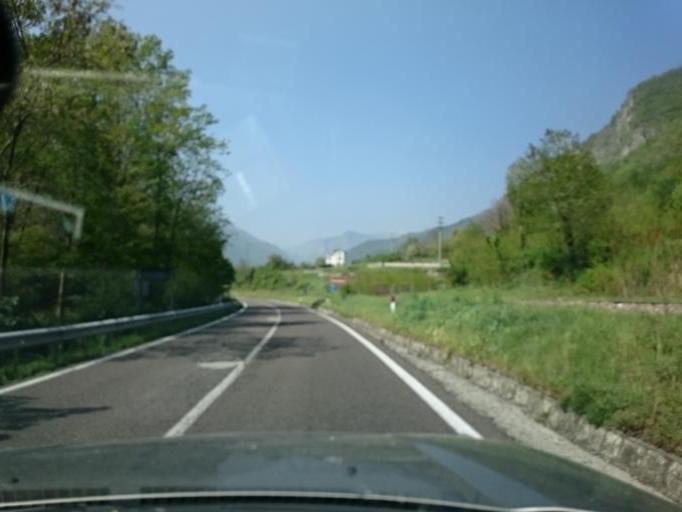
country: IT
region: Veneto
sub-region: Provincia di Vicenza
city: Campolongo sul Brenta
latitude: 45.8315
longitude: 11.7014
